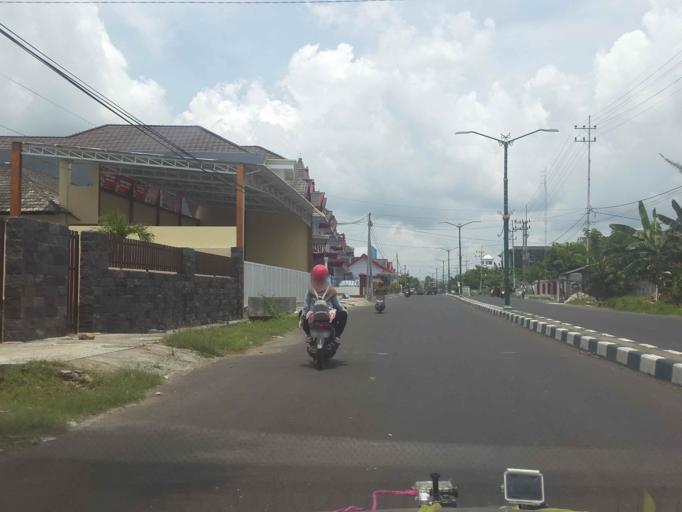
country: ID
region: East Java
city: Sumenep
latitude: -7.0305
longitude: 113.8523
